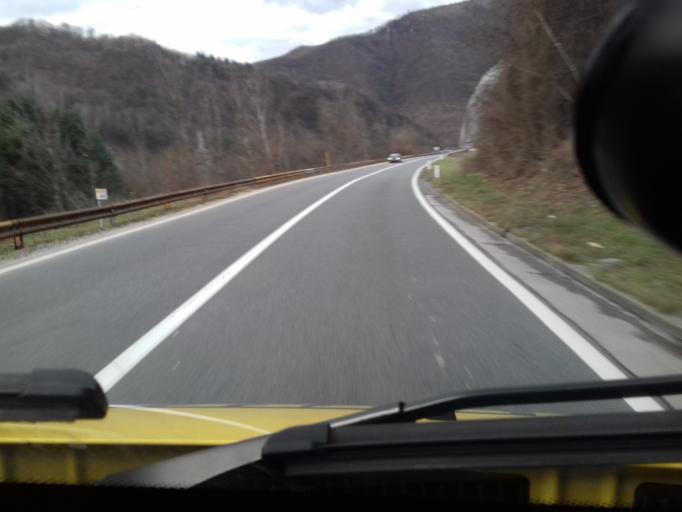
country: BA
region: Federation of Bosnia and Herzegovina
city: Kacuni
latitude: 44.1307
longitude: 17.9409
